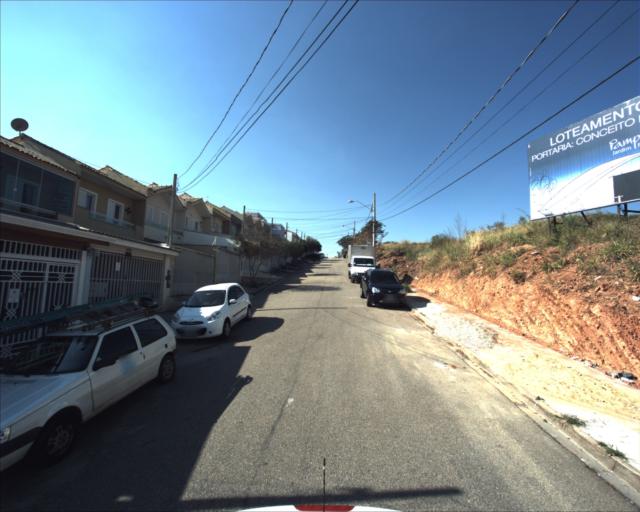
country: BR
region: Sao Paulo
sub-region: Sorocaba
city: Sorocaba
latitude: -23.4985
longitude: -47.4221
